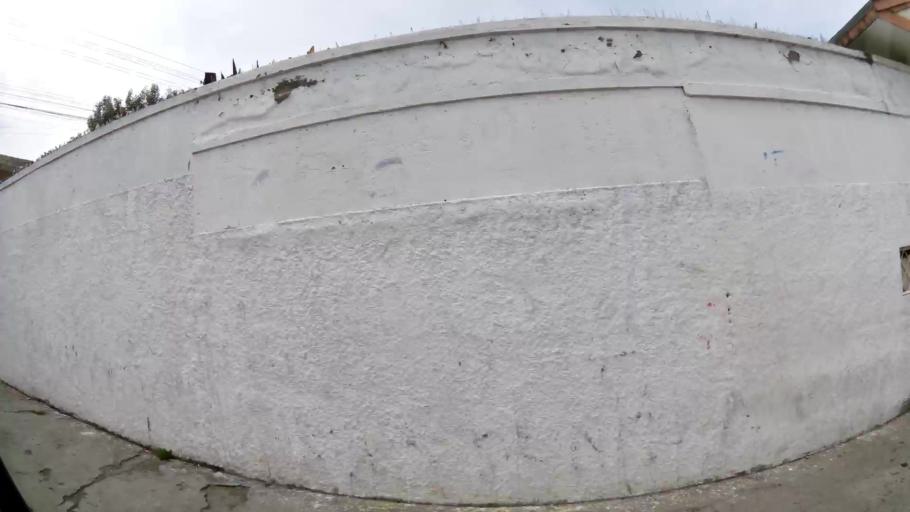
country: EC
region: Cotopaxi
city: Latacunga
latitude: -0.9349
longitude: -78.6120
